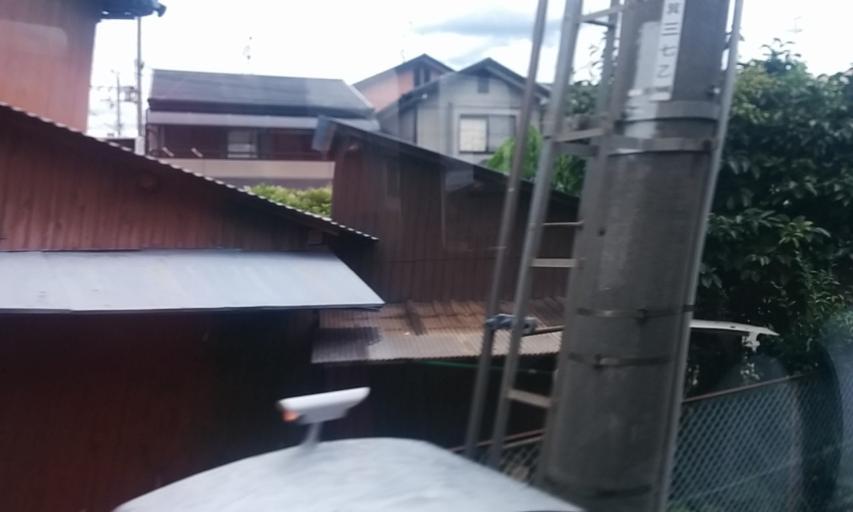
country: JP
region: Osaka
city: Mino
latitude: 34.8158
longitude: 135.4585
